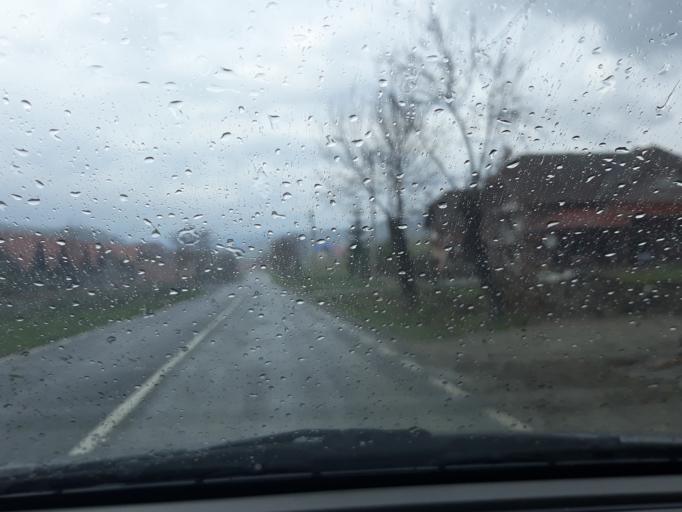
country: RO
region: Harghita
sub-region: Comuna Corund
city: Corund
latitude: 46.4820
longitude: 25.1719
